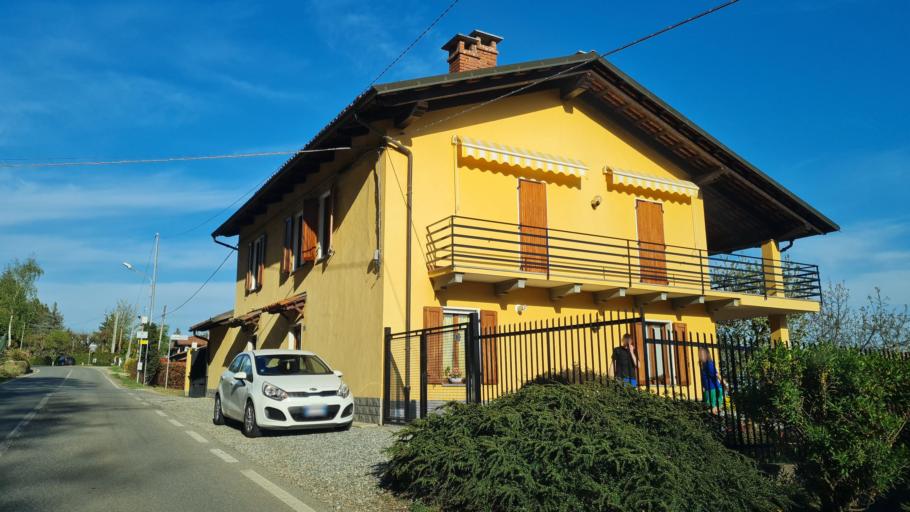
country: IT
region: Piedmont
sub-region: Provincia di Biella
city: Pollone
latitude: 45.5791
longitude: 7.9906
